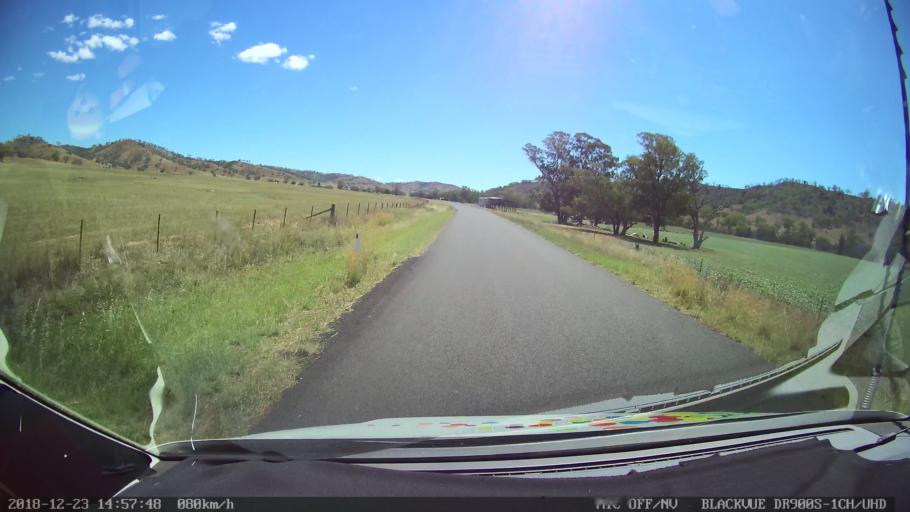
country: AU
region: New South Wales
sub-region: Tamworth Municipality
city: Manilla
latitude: -30.7116
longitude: 150.8200
